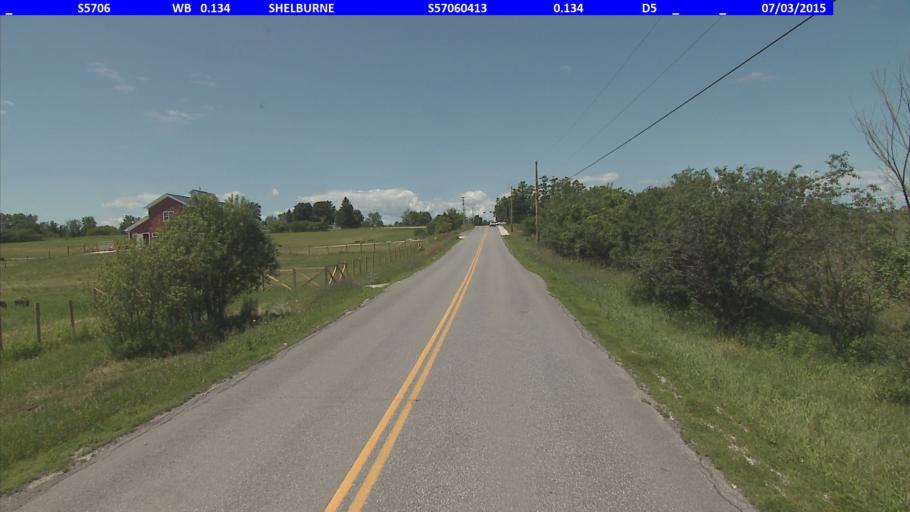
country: US
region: Vermont
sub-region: Chittenden County
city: South Burlington
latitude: 44.4075
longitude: -73.1755
